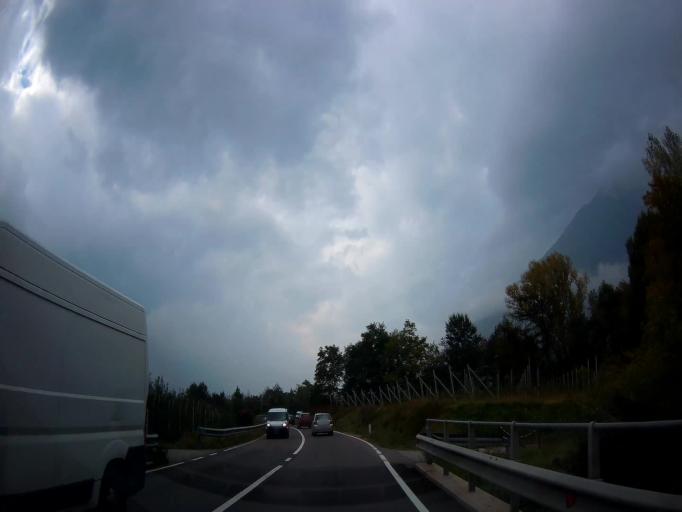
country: IT
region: Trentino-Alto Adige
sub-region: Bolzano
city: Rabla
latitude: 46.6719
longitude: 11.0714
